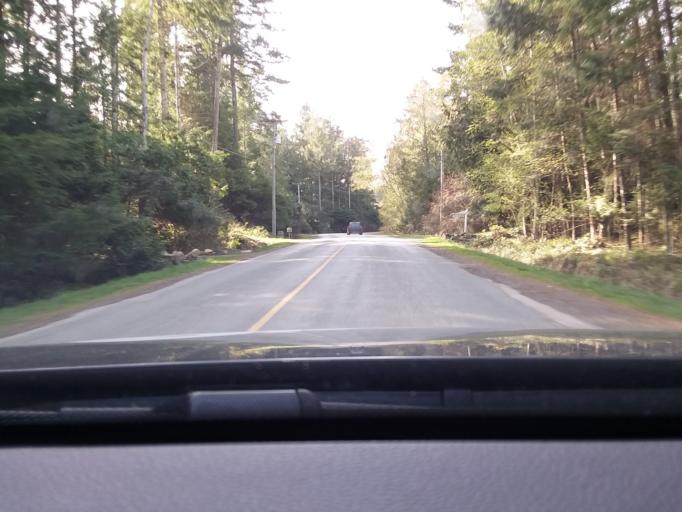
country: CA
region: British Columbia
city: North Saanich
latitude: 48.7643
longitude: -123.2823
